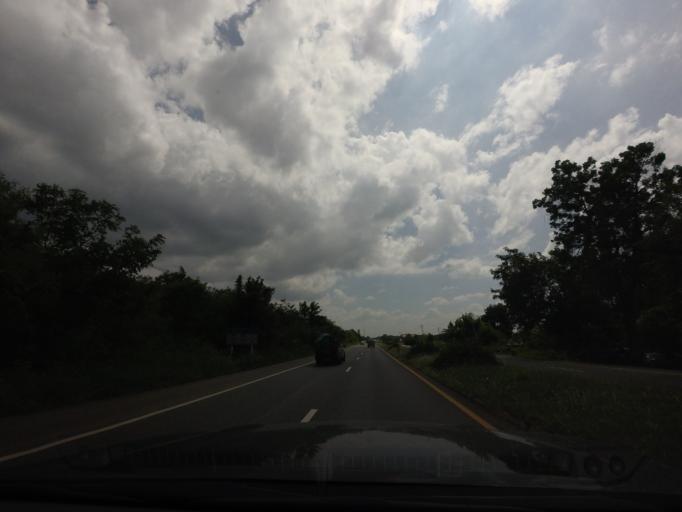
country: TH
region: Phetchabun
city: Phetchabun
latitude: 16.2099
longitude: 101.0890
